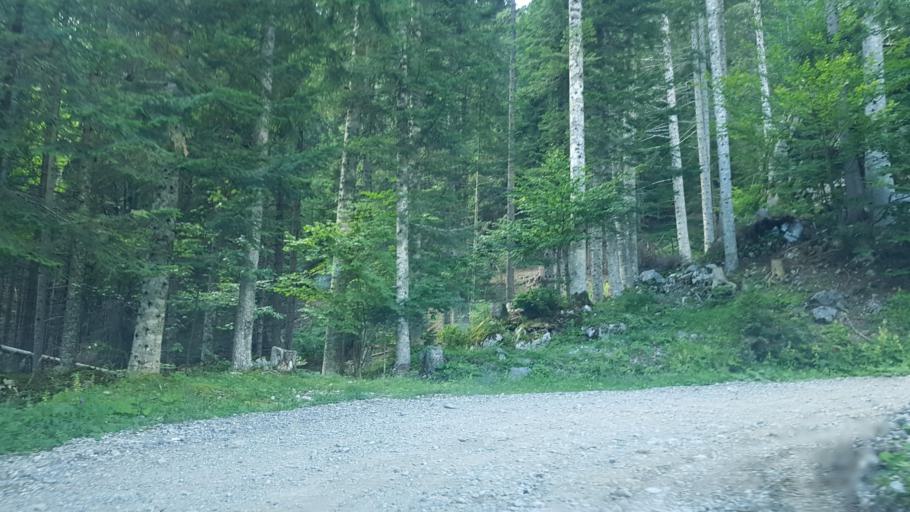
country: IT
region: Friuli Venezia Giulia
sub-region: Provincia di Udine
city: Forni Avoltri
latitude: 46.5885
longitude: 12.7973
